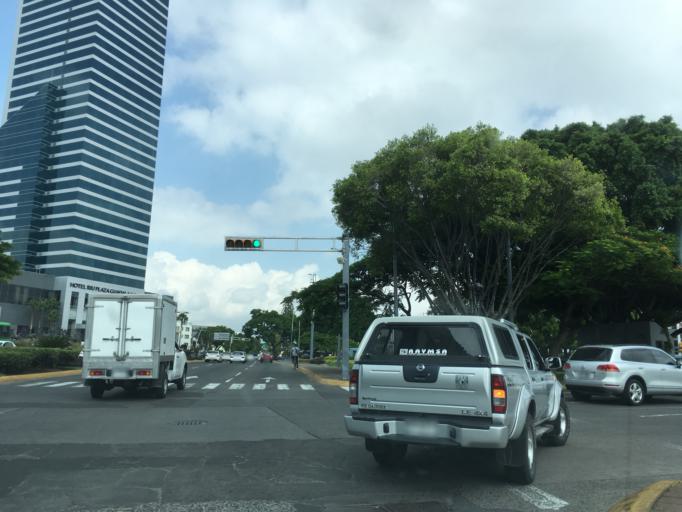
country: MX
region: Jalisco
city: Guadalajara
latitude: 20.6666
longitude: -103.3918
